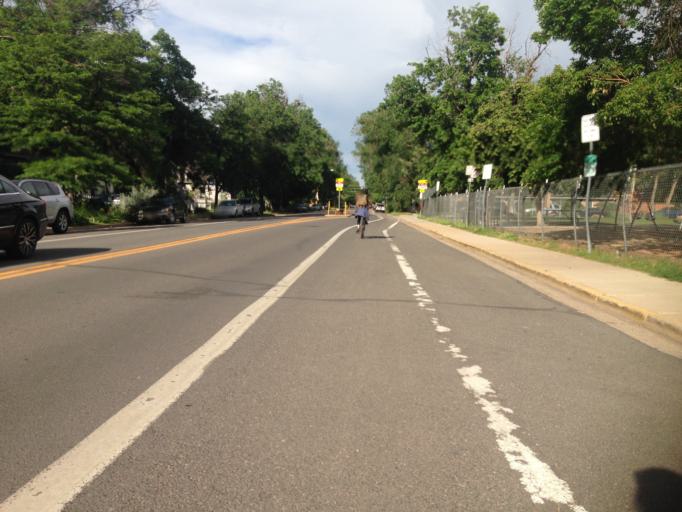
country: US
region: Colorado
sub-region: Boulder County
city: Boulder
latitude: 40.0221
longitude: -105.2698
